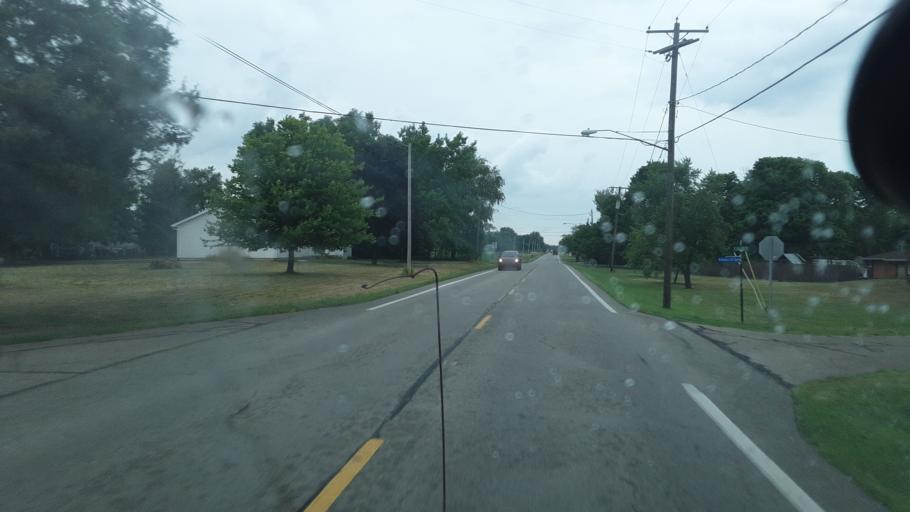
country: US
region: Ohio
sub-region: Williams County
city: Bryan
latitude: 41.4302
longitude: -84.6088
